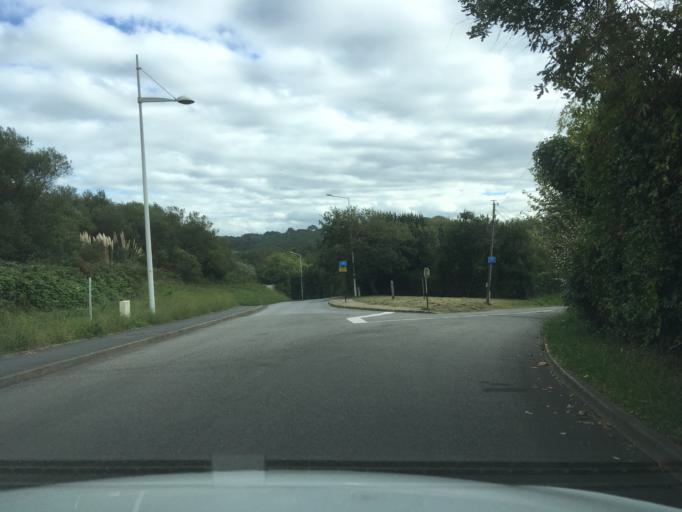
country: FR
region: Aquitaine
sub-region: Departement des Pyrenees-Atlantiques
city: Biarritz
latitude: 43.4611
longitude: -1.5694
